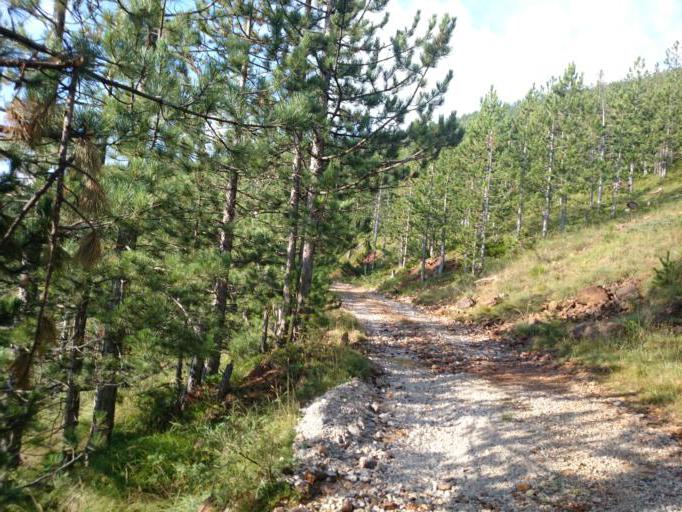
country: AL
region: Diber
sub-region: Rrethi i Dibres
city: Fushe-Lure
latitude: 41.7984
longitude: 20.2133
